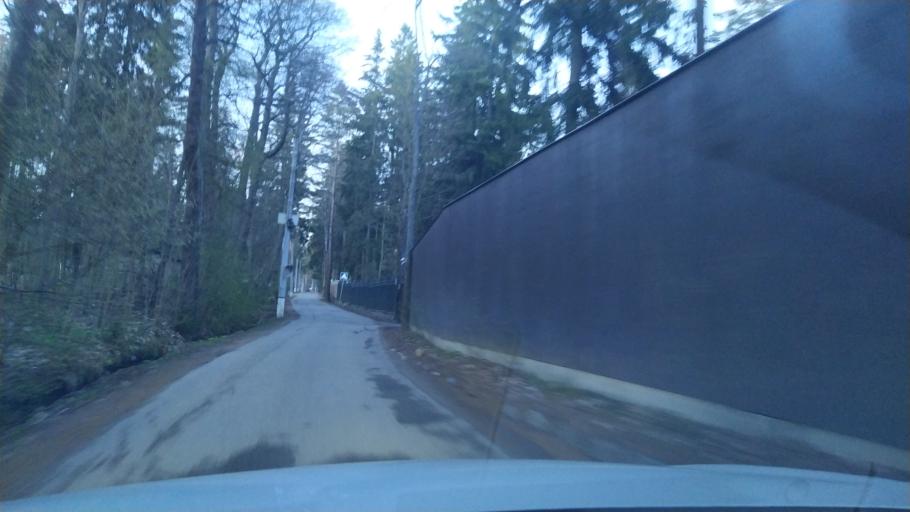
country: RU
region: St.-Petersburg
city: Solnechnoye
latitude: 60.1470
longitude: 29.9286
